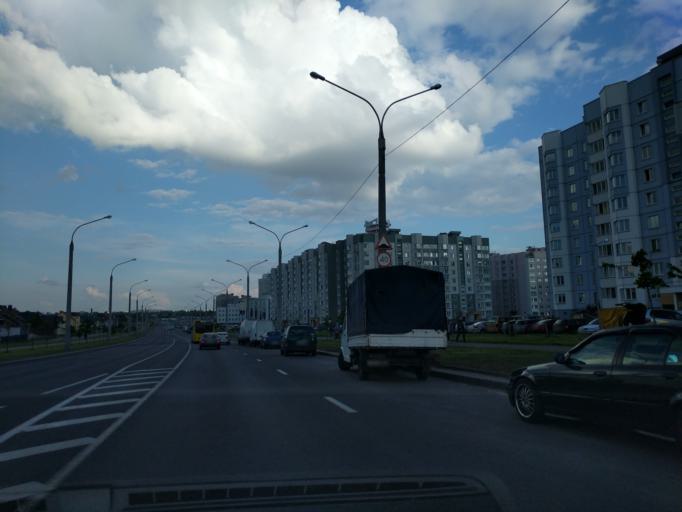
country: BY
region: Minsk
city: Zhdanovichy
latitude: 53.9340
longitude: 27.4358
